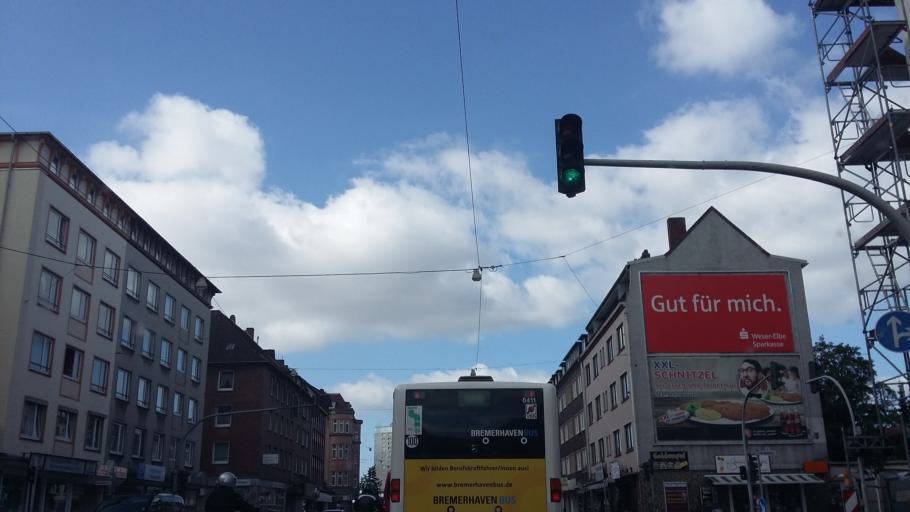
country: DE
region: Bremen
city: Bremerhaven
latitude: 53.5317
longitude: 8.5896
